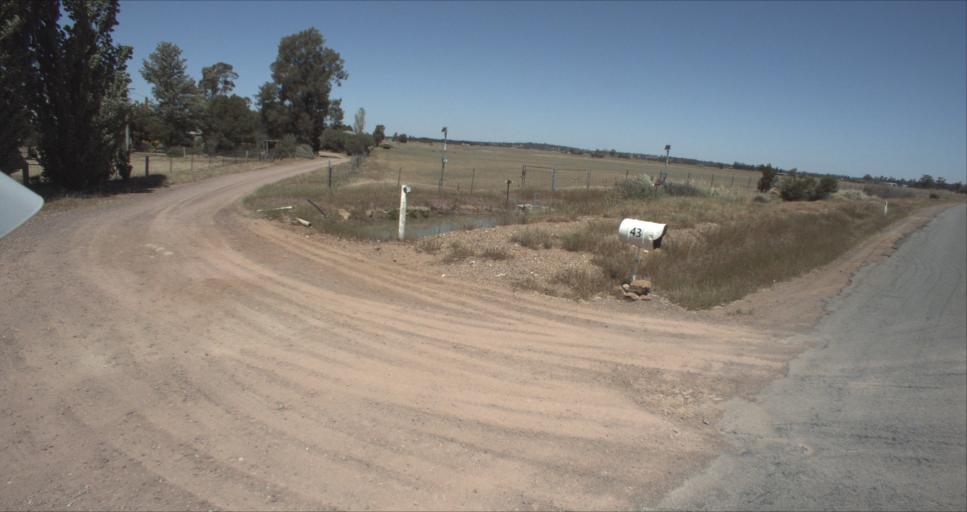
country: AU
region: New South Wales
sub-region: Leeton
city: Leeton
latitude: -34.5383
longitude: 146.4424
